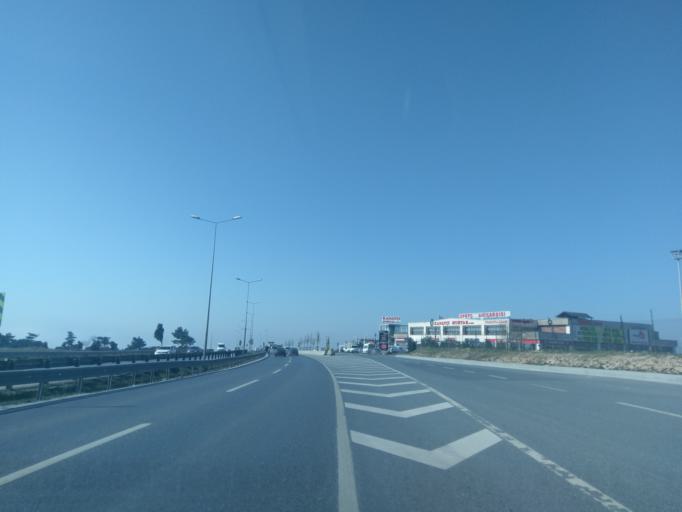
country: TR
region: Istanbul
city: Gurpinar
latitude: 41.0252
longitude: 28.6207
